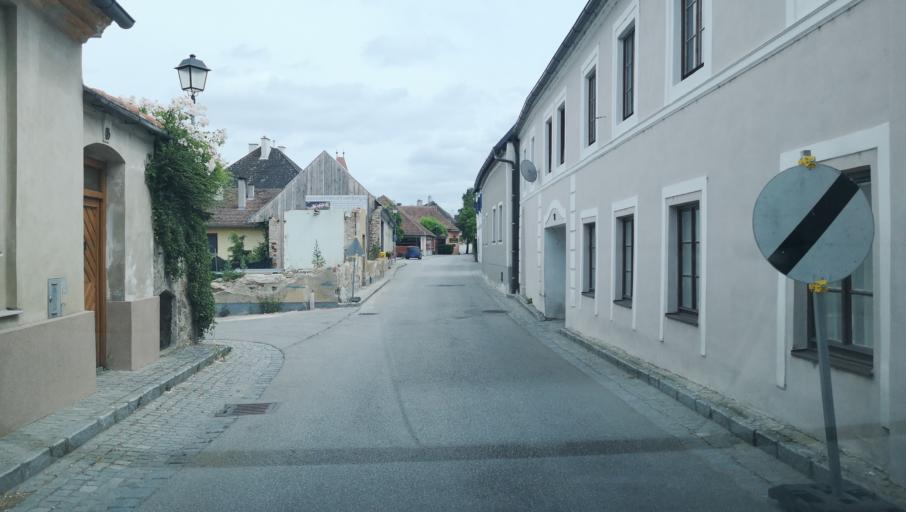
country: AT
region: Lower Austria
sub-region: Politischer Bezirk Krems
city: Durnstein
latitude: 48.3972
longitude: 15.5026
